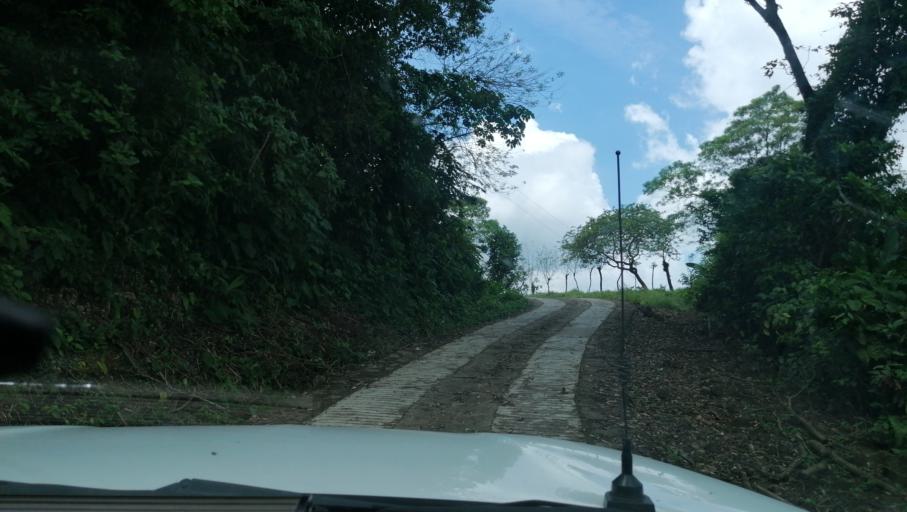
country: MX
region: Chiapas
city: Pichucalco
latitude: 17.4496
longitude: -93.1997
